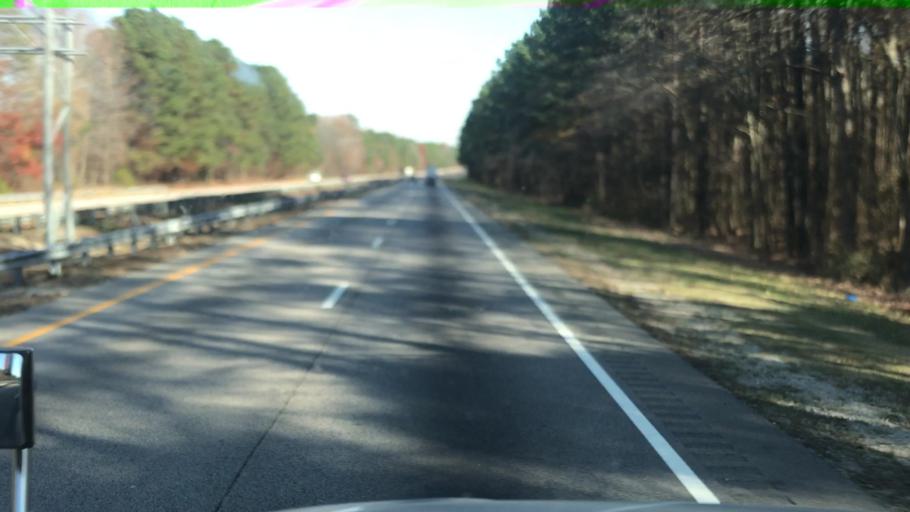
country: US
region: North Carolina
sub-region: Wake County
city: Wendell
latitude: 35.8196
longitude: -78.3924
